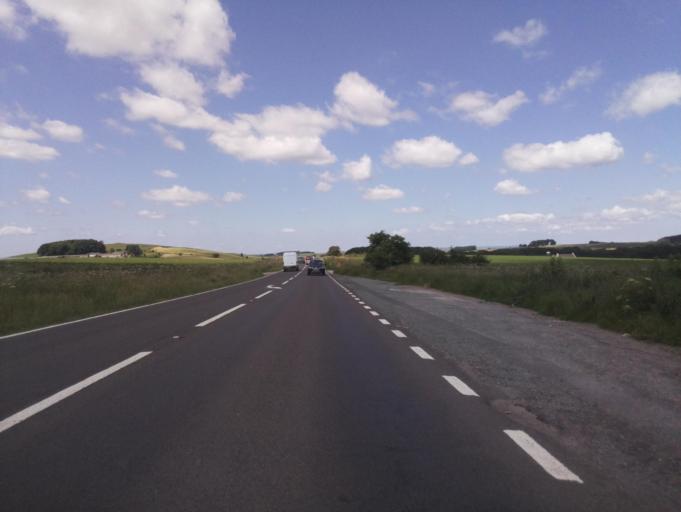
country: GB
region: England
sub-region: Derbyshire
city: Bakewell
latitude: 53.1511
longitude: -1.7676
